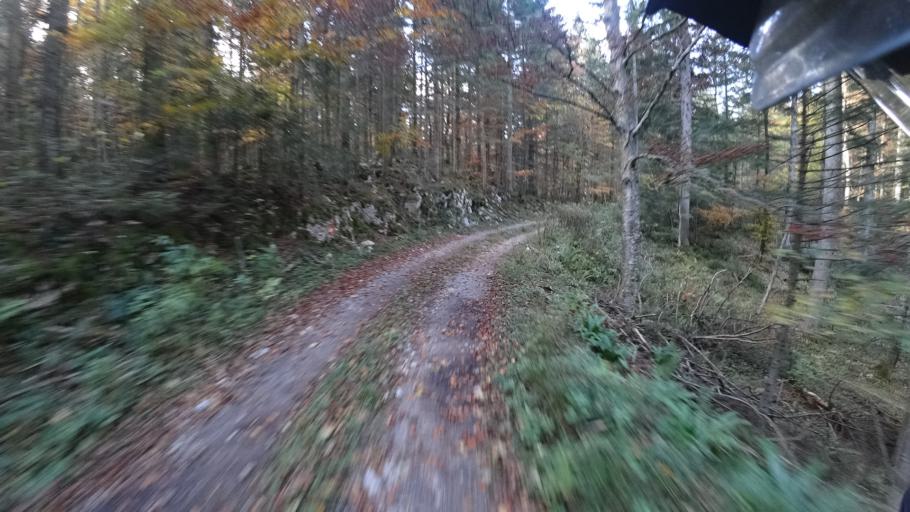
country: HR
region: Karlovacka
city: Plaski
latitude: 45.0433
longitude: 15.3356
